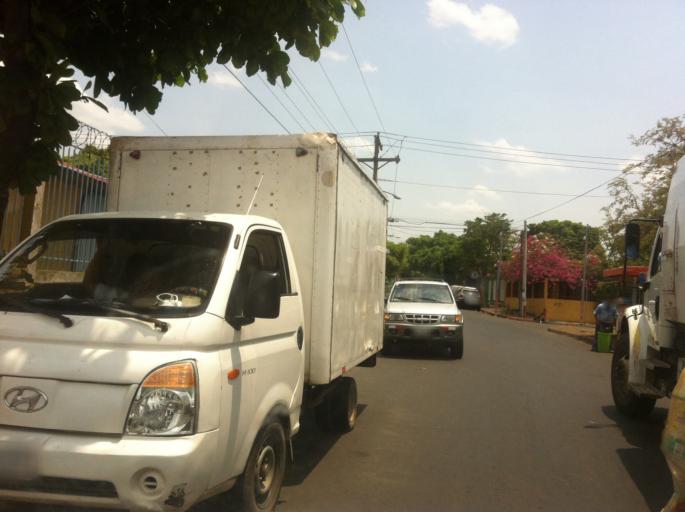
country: NI
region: Managua
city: Managua
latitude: 12.1191
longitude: -86.2503
